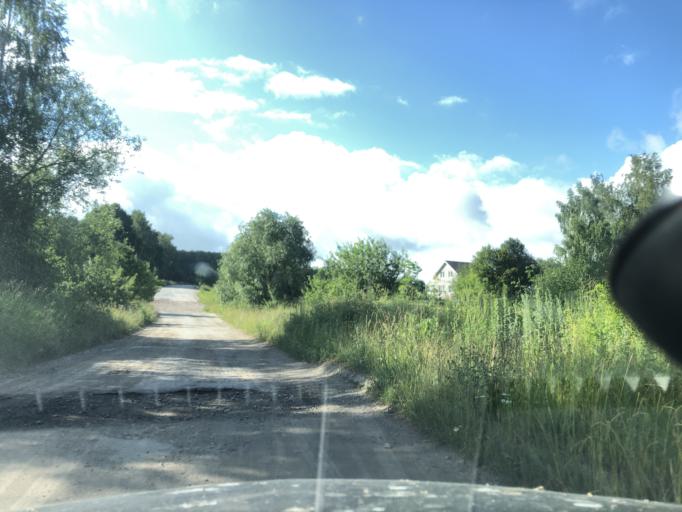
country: RU
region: Tula
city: Shvartsevskiy
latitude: 54.2517
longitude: 37.9288
